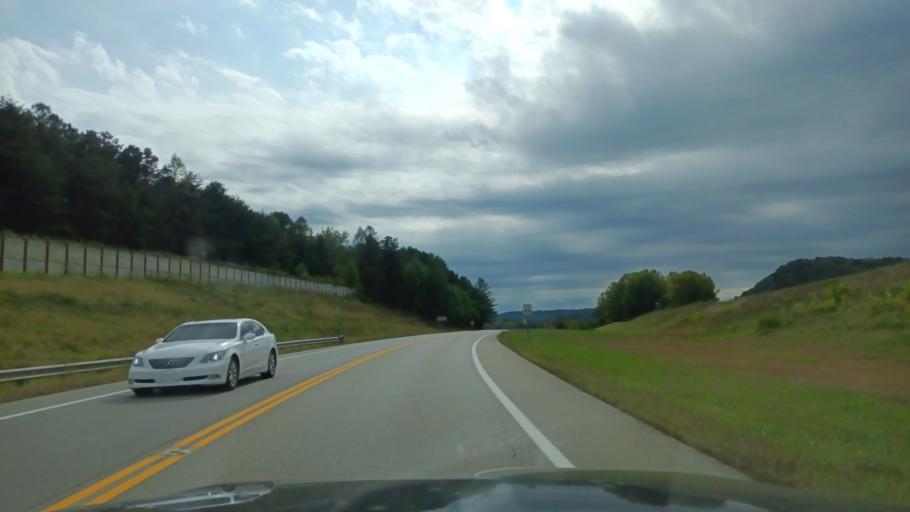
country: US
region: Ohio
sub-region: Jackson County
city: Wellston
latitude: 39.2612
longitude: -82.6820
